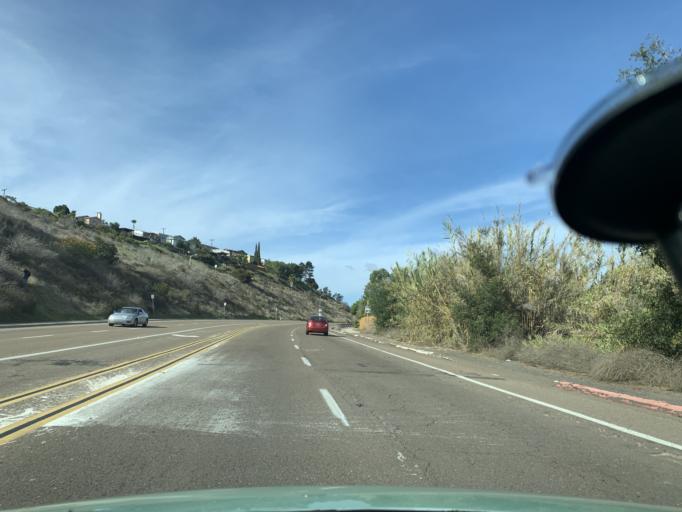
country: US
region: California
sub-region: San Diego County
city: San Diego
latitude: 32.8053
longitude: -117.1755
